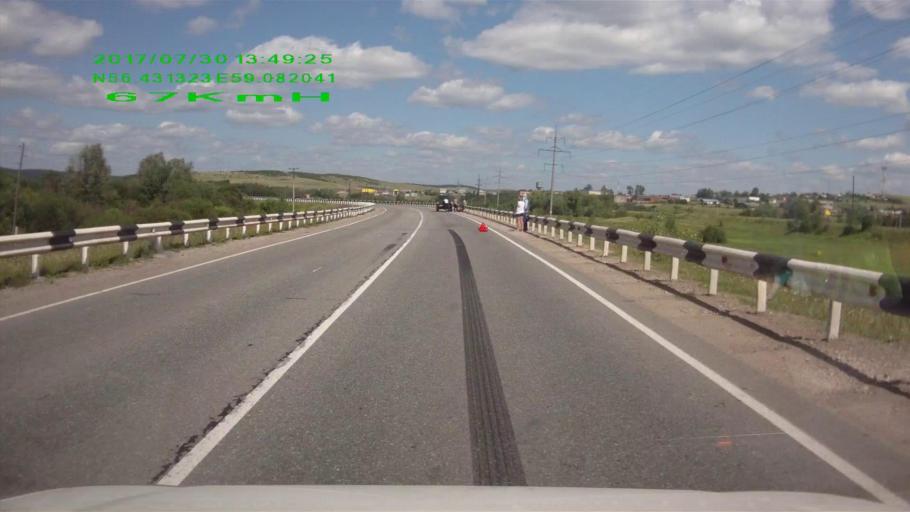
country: RU
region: Sverdlovsk
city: Mikhaylovsk
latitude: 56.4315
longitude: 59.0823
